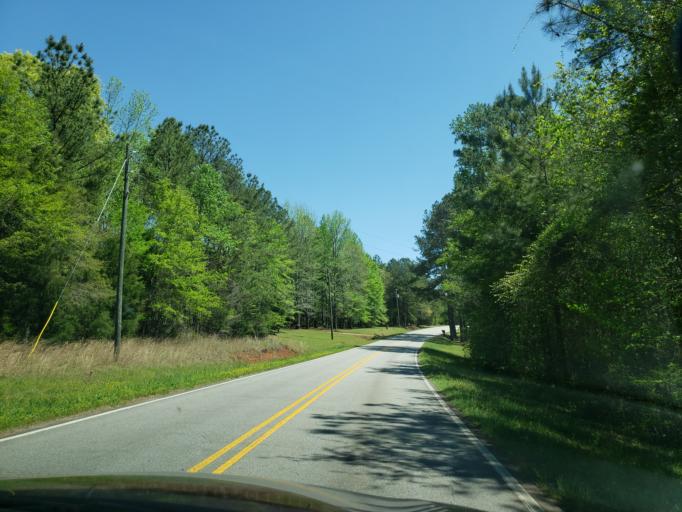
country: US
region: Alabama
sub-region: Tallapoosa County
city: Camp Hill
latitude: 32.7023
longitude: -85.7109
